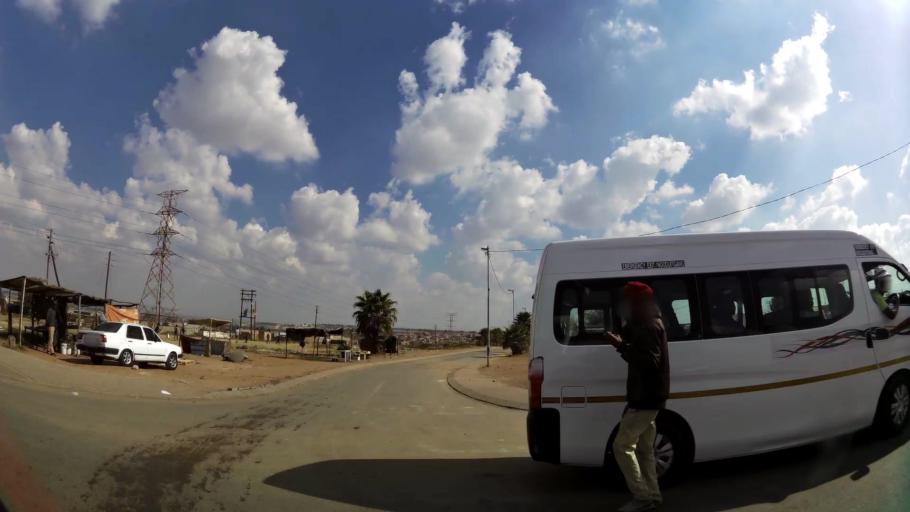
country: ZA
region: Gauteng
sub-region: City of Johannesburg Metropolitan Municipality
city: Roodepoort
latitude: -26.1948
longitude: 27.8683
